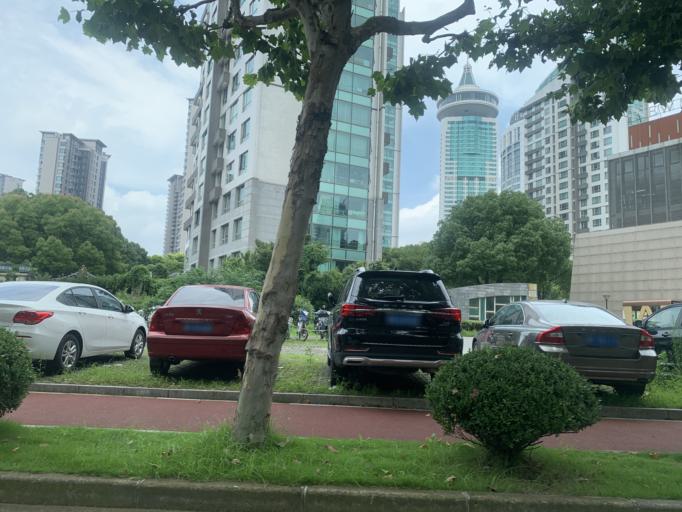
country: CN
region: Shanghai Shi
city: Huamu
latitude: 31.2118
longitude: 121.5332
